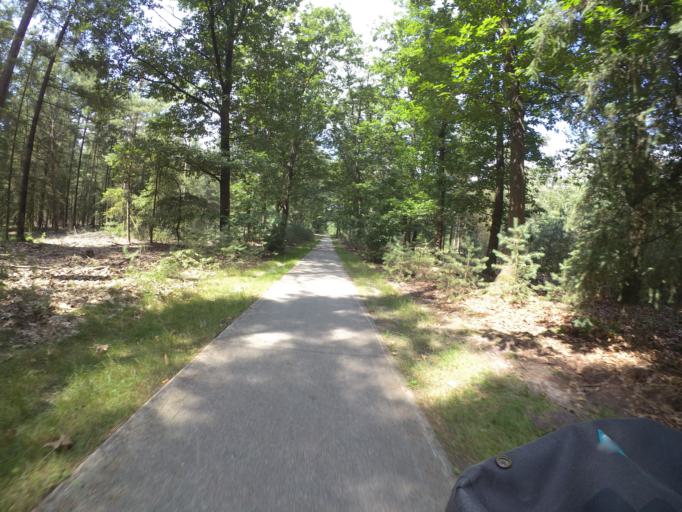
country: NL
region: Gelderland
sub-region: Gemeente Heerde
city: Heerde
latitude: 52.4147
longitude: 6.0249
